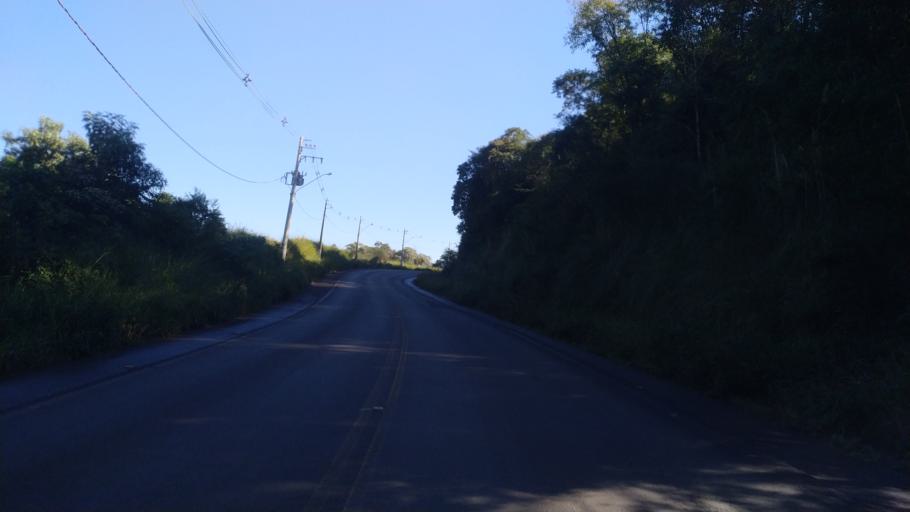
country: BR
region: Santa Catarina
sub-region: Chapeco
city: Chapeco
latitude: -27.1293
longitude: -52.6283
